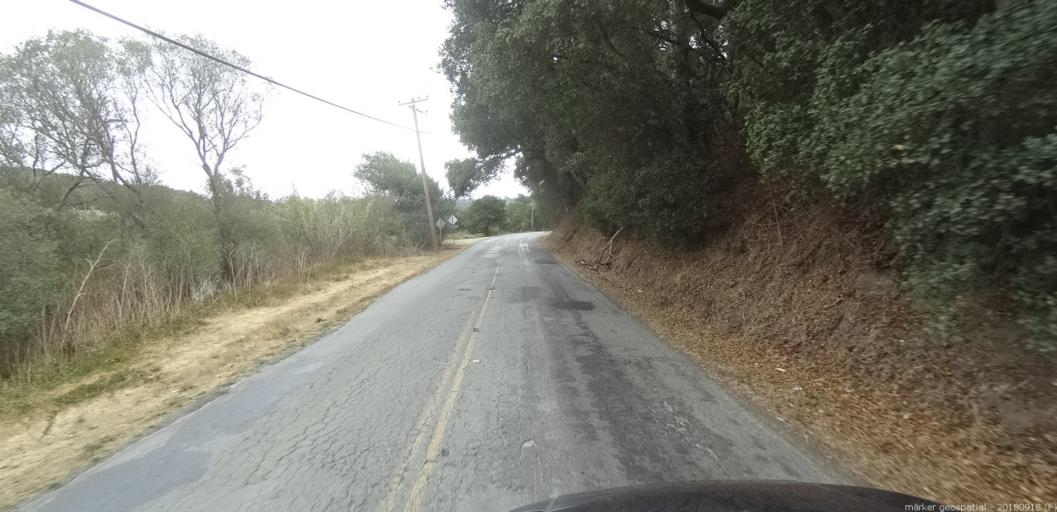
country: US
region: California
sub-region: Monterey County
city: Prunedale
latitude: 36.7784
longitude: -121.6489
